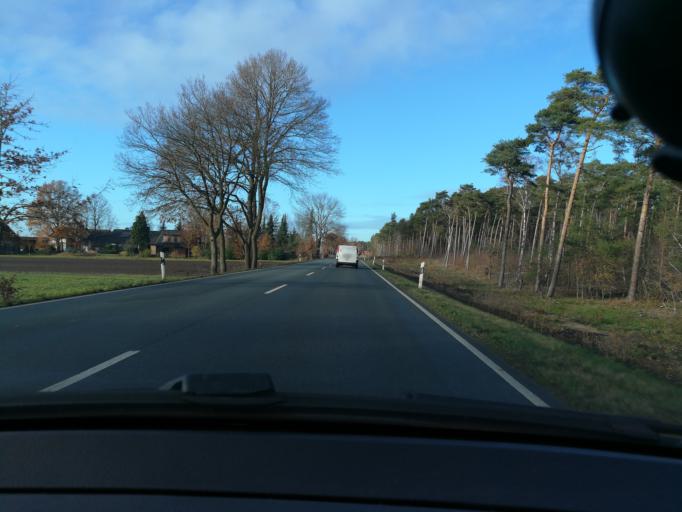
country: DE
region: Lower Saxony
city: Uchte
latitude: 52.5388
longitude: 8.8709
